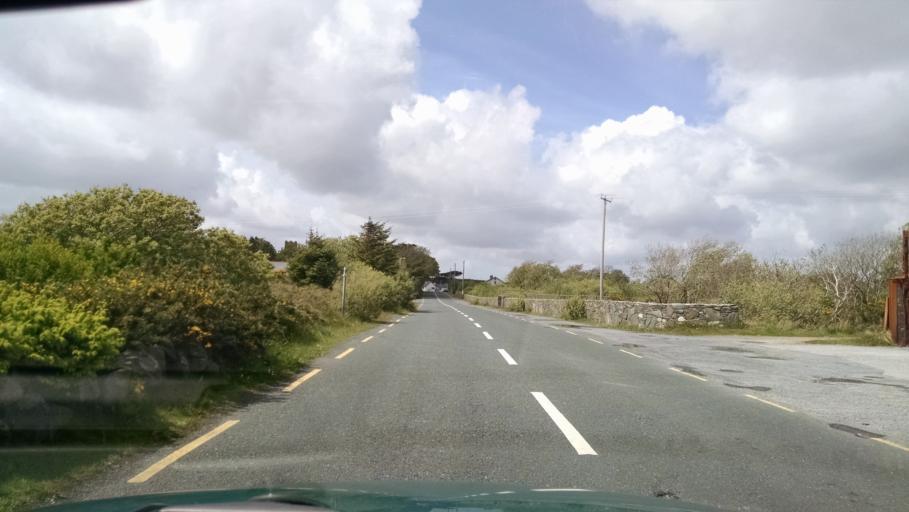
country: IE
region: Connaught
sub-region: County Galway
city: Clifden
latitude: 53.3224
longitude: -9.8143
